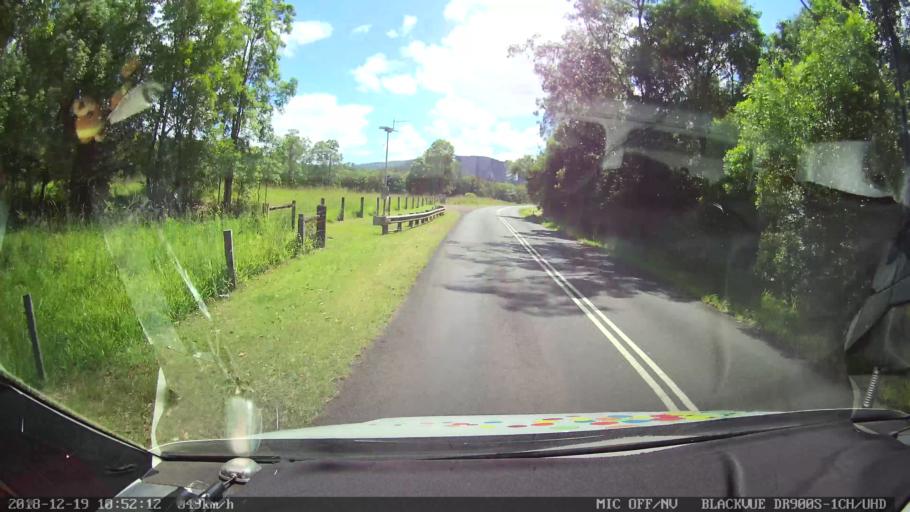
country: AU
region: New South Wales
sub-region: Lismore Municipality
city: Nimbin
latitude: -28.5929
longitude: 153.2277
